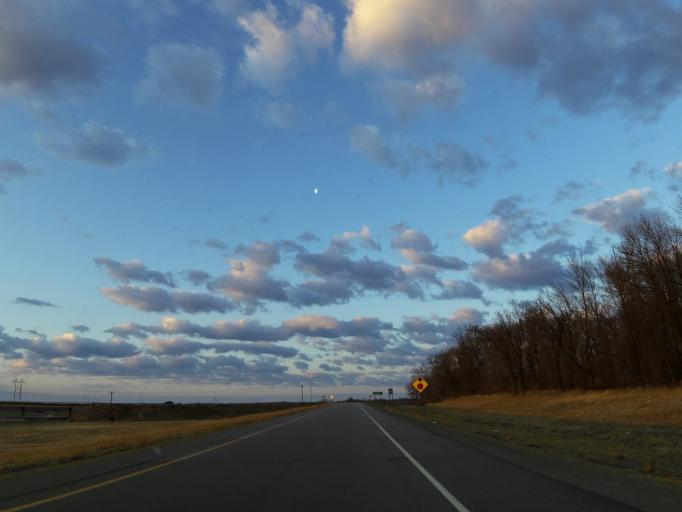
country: US
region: Minnesota
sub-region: Rice County
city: Dundas
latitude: 44.4308
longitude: -93.2934
